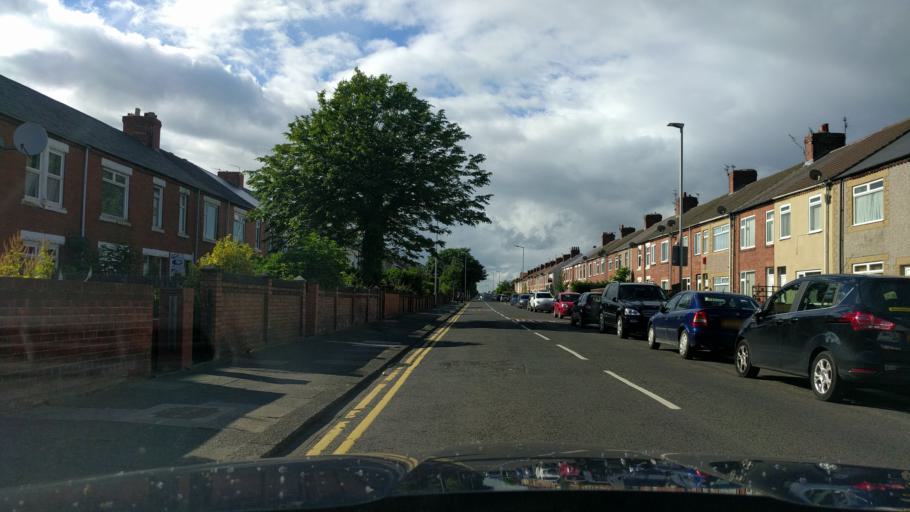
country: GB
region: England
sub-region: Northumberland
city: Ashington
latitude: 55.1775
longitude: -1.5595
